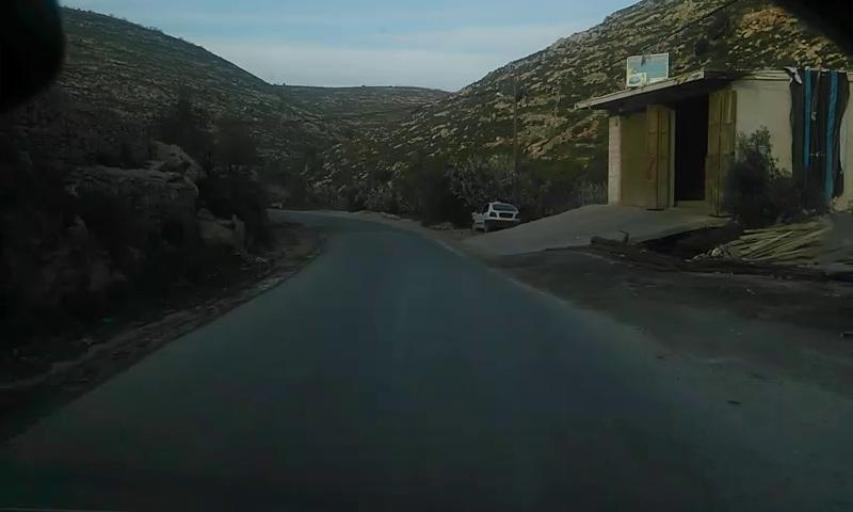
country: PS
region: West Bank
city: Ash Shuyukh
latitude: 31.5915
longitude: 35.1593
